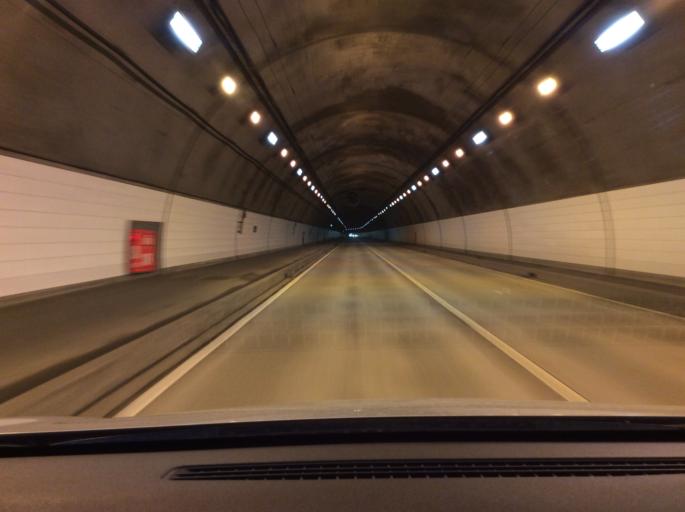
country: JP
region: Fukushima
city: Iwaki
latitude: 37.0850
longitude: 140.7815
